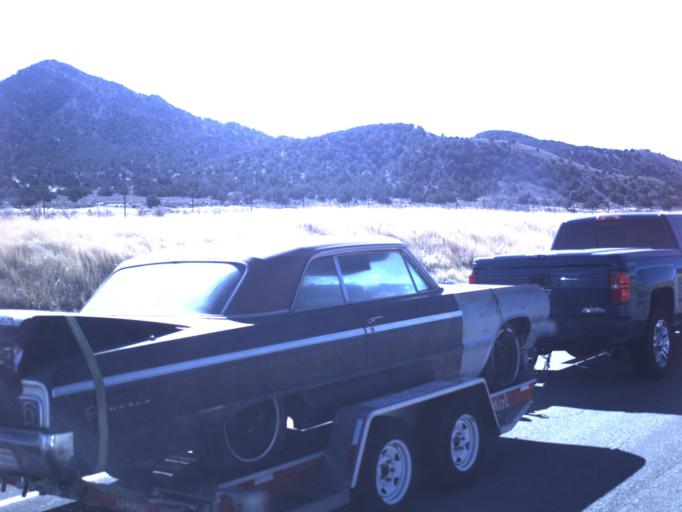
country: US
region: Utah
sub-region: Sanpete County
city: Gunnison
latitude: 39.4245
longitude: -111.9207
